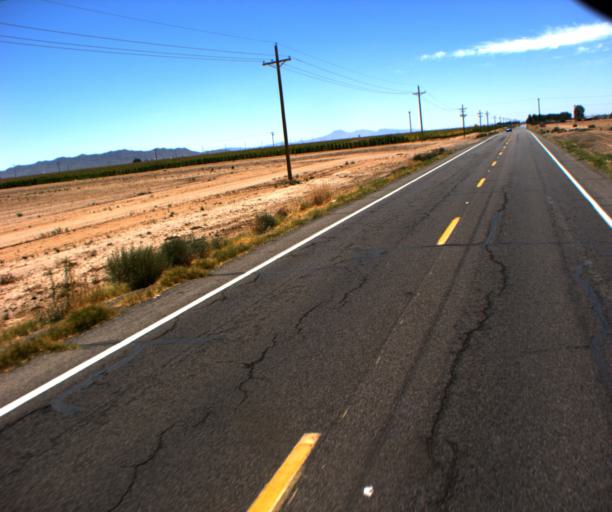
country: US
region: Arizona
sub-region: Pinal County
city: Arizona City
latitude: 32.8797
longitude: -111.6155
